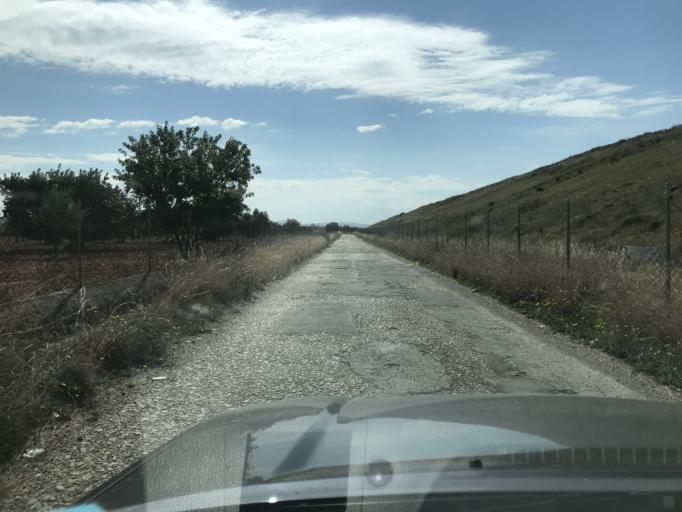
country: ES
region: Balearic Islands
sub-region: Illes Balears
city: Bunyola
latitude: 39.6480
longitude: 2.6845
